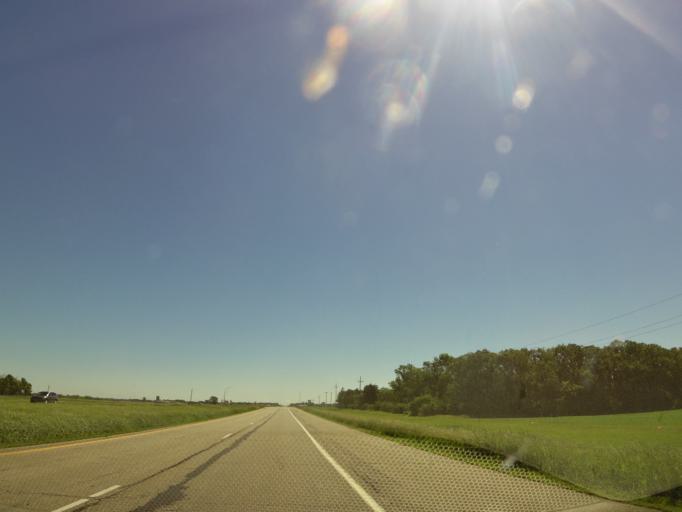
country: US
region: Minnesota
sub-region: Polk County
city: Crookston
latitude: 47.7604
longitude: -96.4640
